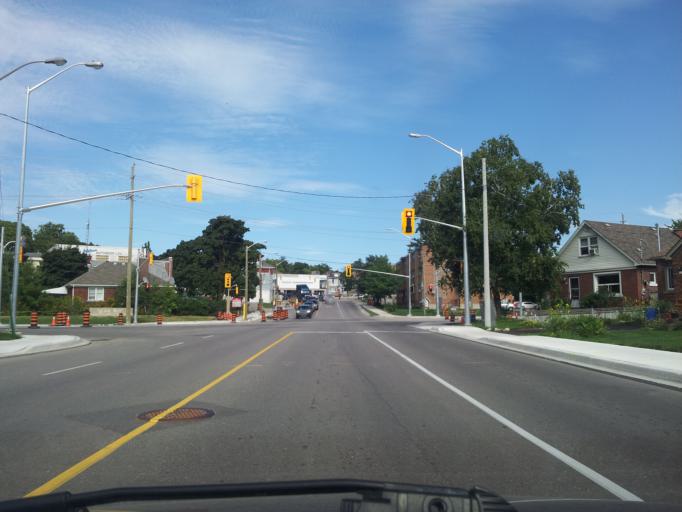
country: CA
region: Ontario
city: Kitchener
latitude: 43.4435
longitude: -80.4788
